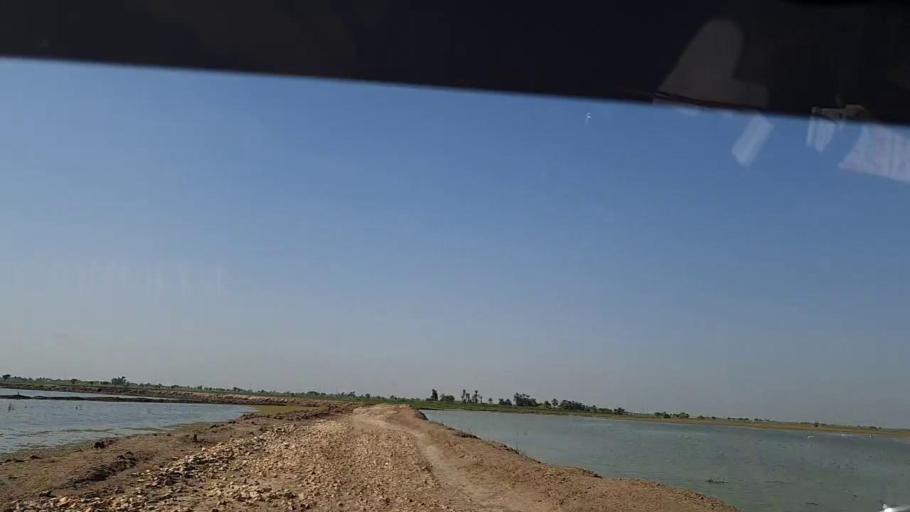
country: PK
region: Sindh
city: Tangwani
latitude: 28.3592
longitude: 69.0370
